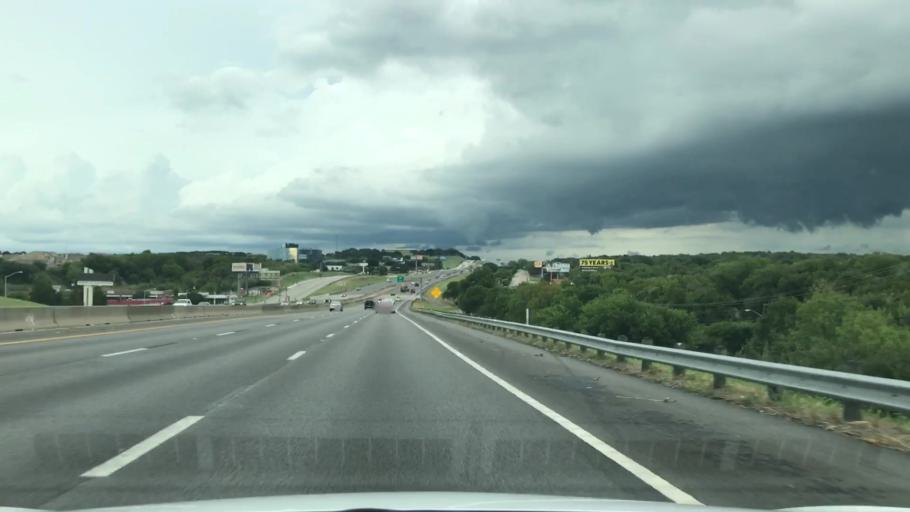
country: US
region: Texas
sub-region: Tarrant County
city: Haltom City
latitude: 32.7600
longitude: -97.2435
